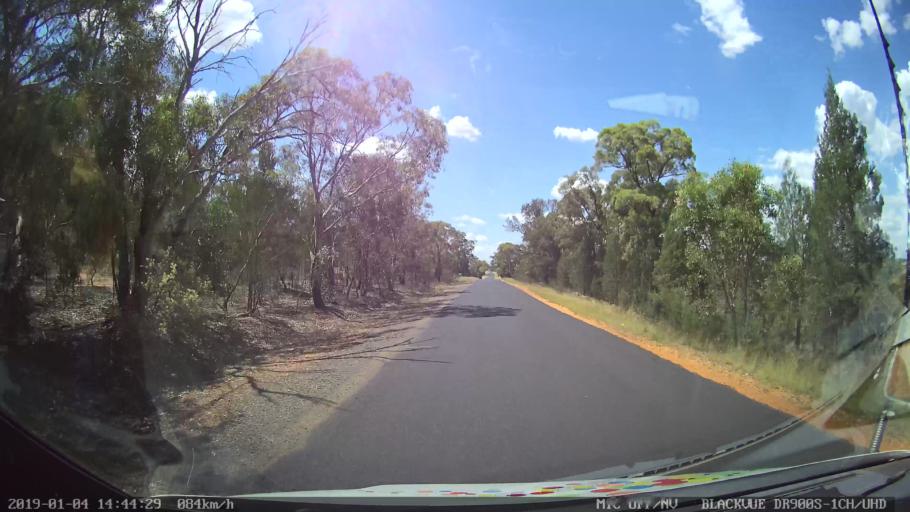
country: AU
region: New South Wales
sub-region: Dubbo Municipality
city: Dubbo
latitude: -32.1057
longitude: 148.6557
